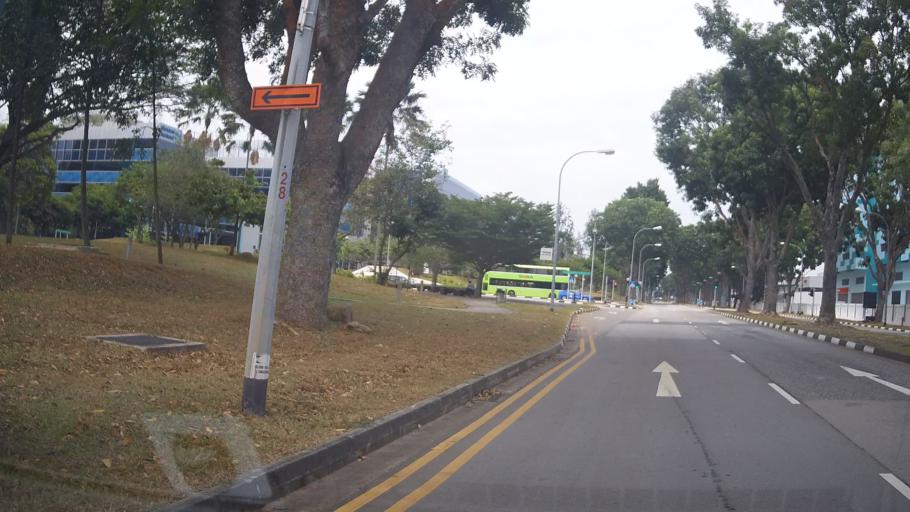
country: SG
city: Singapore
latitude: 1.3323
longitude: 103.9678
